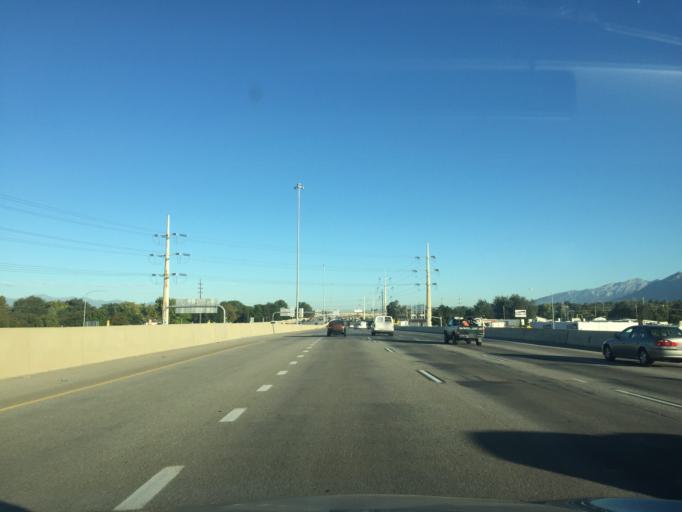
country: US
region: Utah
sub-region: Utah County
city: Provo
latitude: 40.2342
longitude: -111.6850
